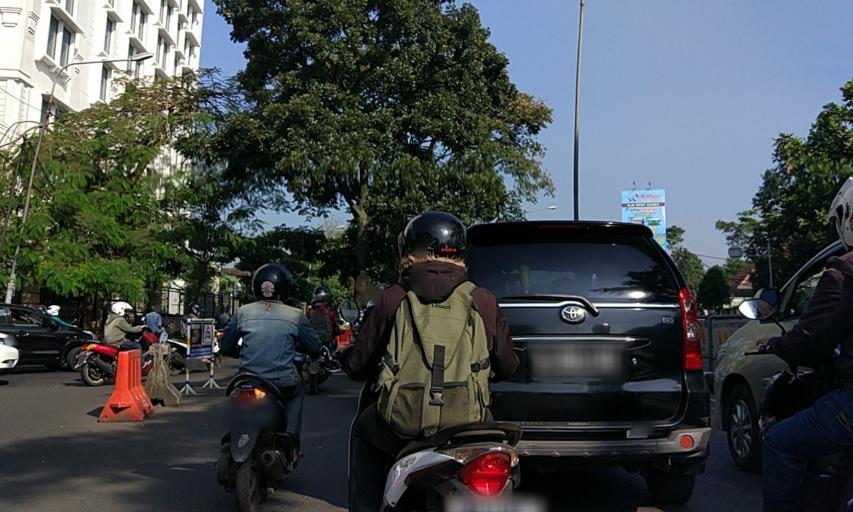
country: ID
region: West Java
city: Bandung
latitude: -6.8995
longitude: 107.6182
